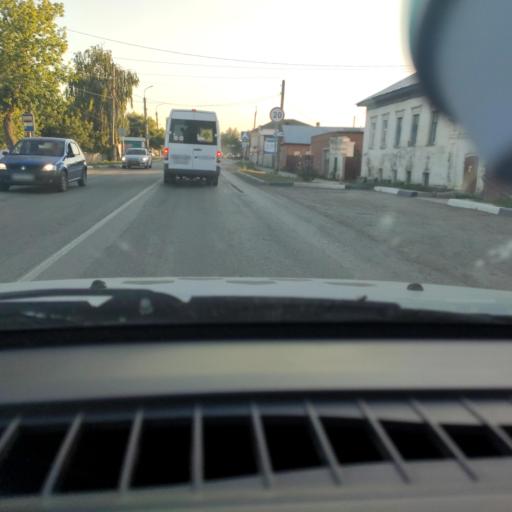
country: RU
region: Perm
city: Kungur
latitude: 57.4336
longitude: 56.9448
